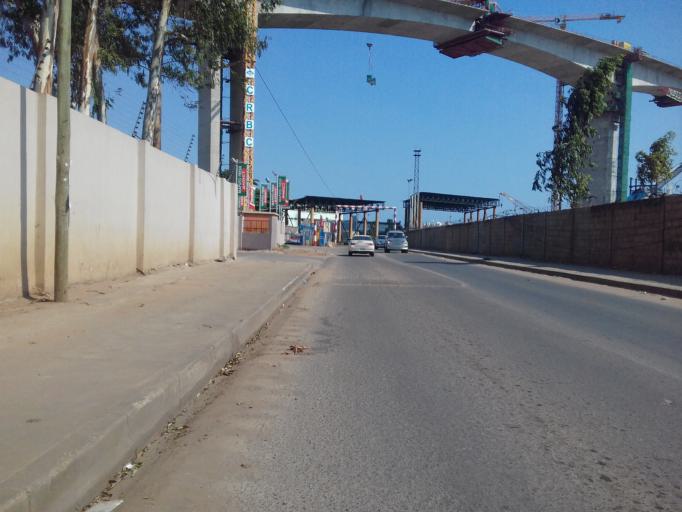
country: MZ
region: Maputo City
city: Maputo
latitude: -25.9652
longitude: 32.5590
